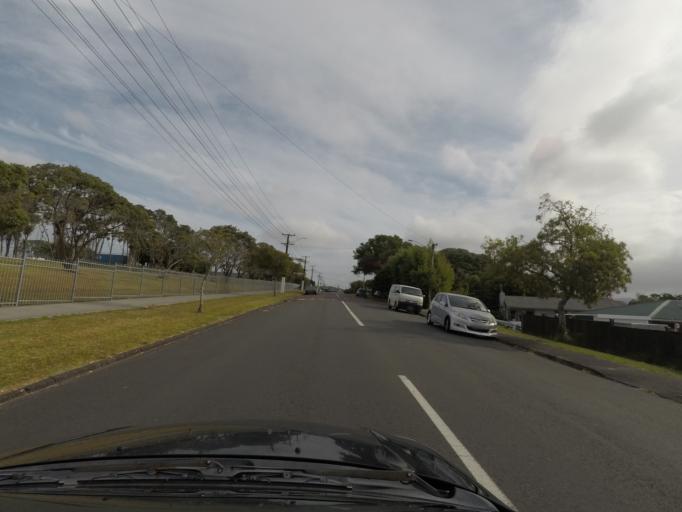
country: NZ
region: Auckland
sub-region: Auckland
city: Waitakere
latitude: -36.9048
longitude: 174.6643
